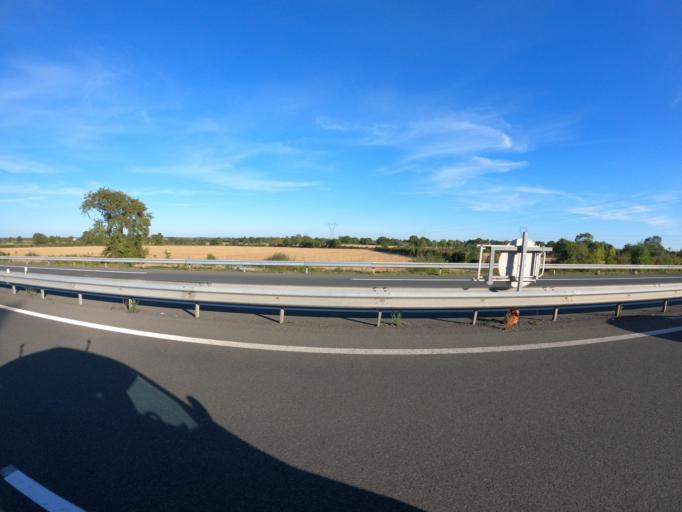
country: FR
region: Pays de la Loire
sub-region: Departement de Maine-et-Loire
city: Saint-Lambert-du-Lattay
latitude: 47.2596
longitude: -0.6169
